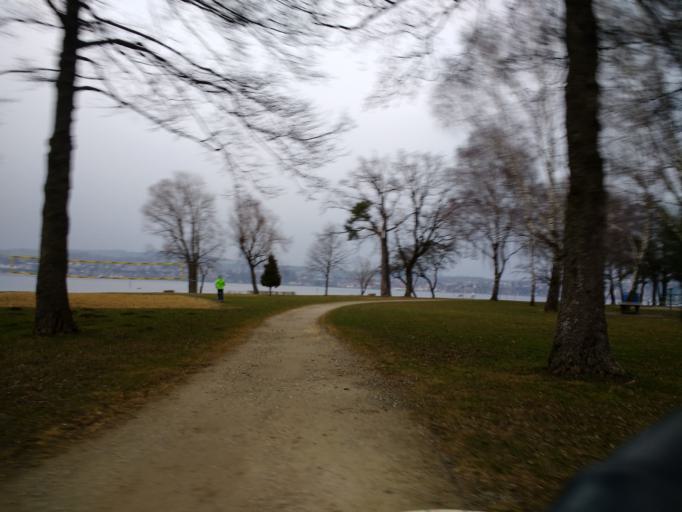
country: DE
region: Baden-Wuerttemberg
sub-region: Tuebingen Region
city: Uberlingen
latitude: 47.7472
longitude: 9.1458
